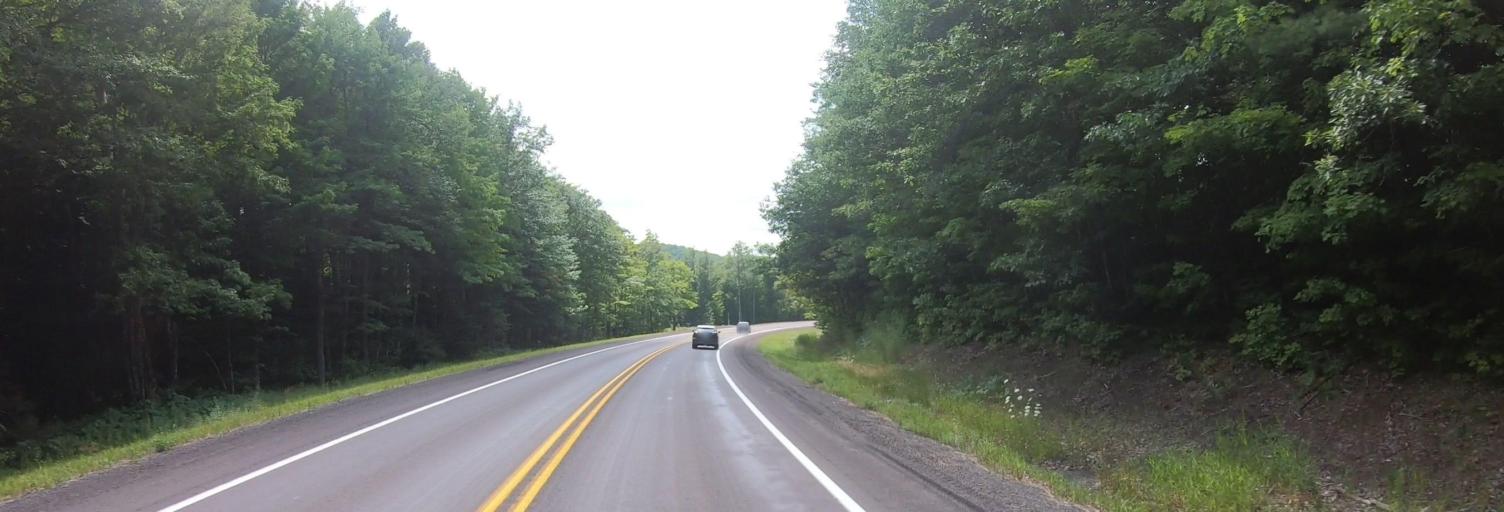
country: US
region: Michigan
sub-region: Houghton County
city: Hancock
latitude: 47.0283
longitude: -88.6965
